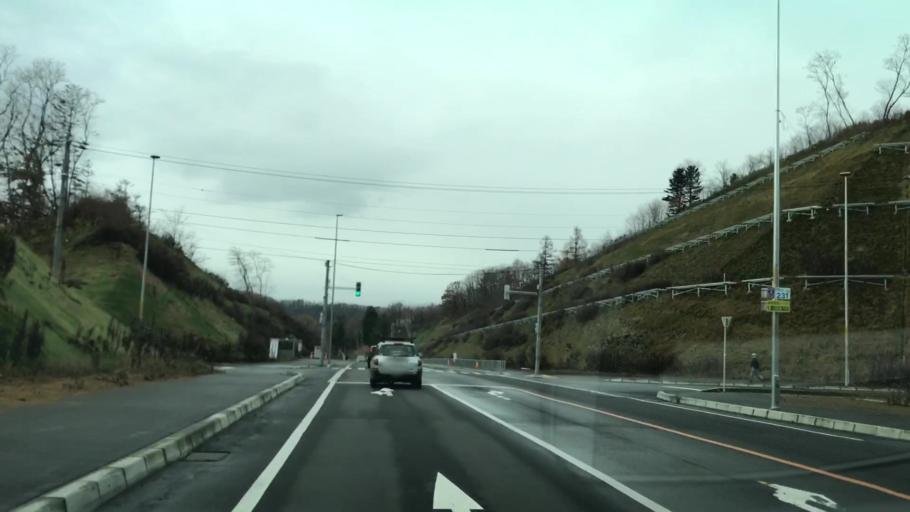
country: JP
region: Hokkaido
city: Yoichi
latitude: 43.2032
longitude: 140.8723
